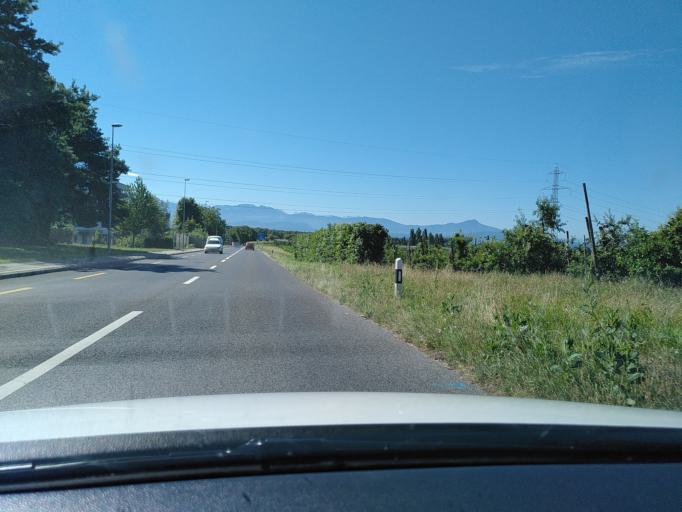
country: CH
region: Vaud
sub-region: Morges District
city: Aubonne
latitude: 46.4850
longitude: 6.4005
